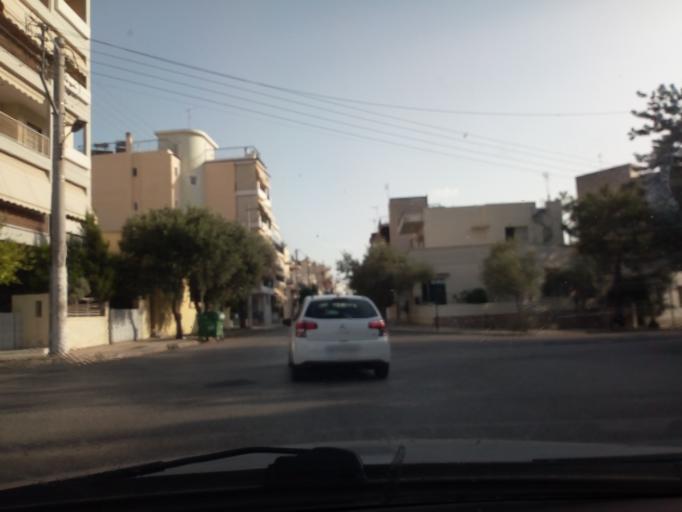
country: GR
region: Attica
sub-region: Nomarchia Athinas
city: Ilioupoli
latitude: 37.9414
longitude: 23.7575
